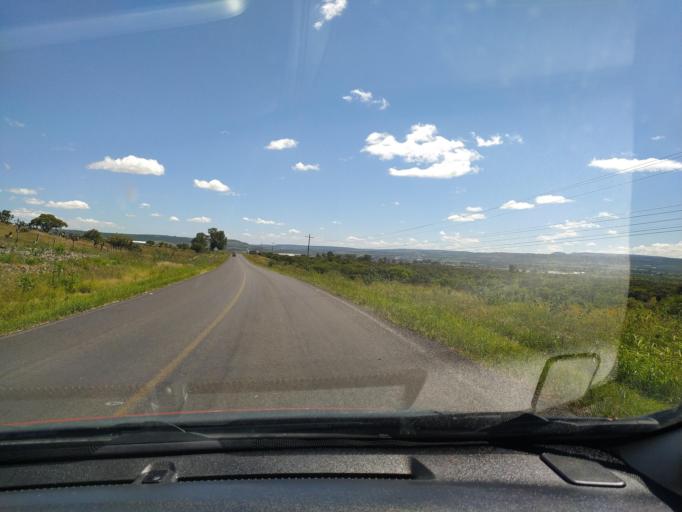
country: MX
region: Jalisco
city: San Miguel el Alto
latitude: 21.0239
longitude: -102.4345
